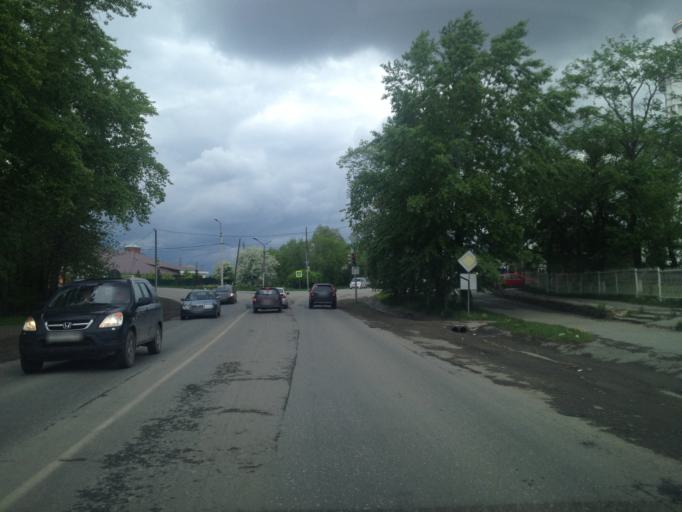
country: RU
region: Sverdlovsk
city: Aramil
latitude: 56.6995
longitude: 60.8303
